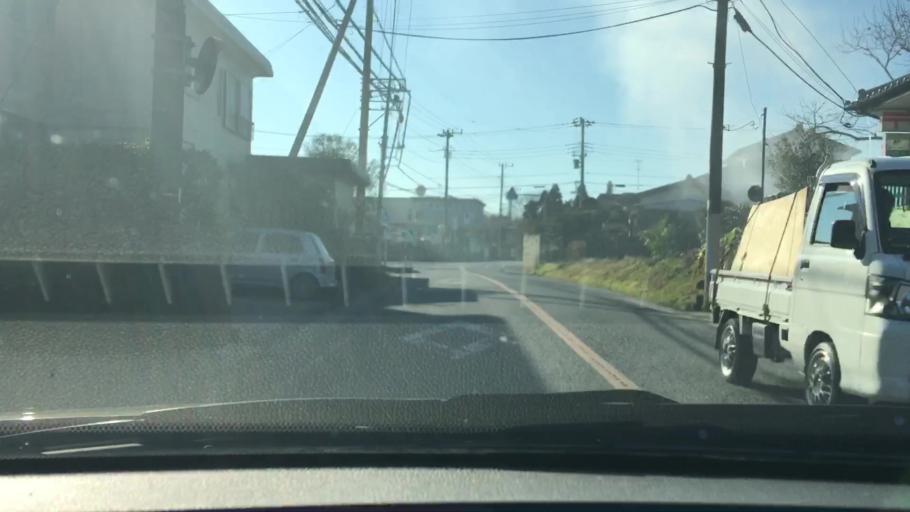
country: JP
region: Chiba
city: Shisui
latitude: 35.6969
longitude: 140.2607
